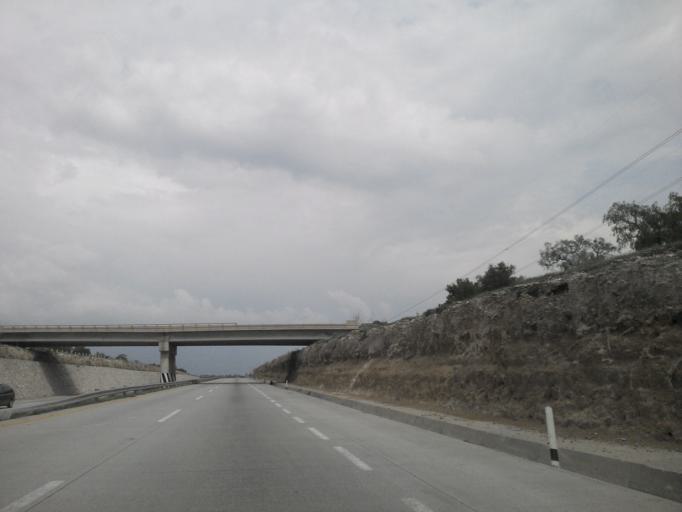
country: MX
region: Mexico
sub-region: Apaxco
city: Colonia Juarez
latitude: 19.9997
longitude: -99.1394
